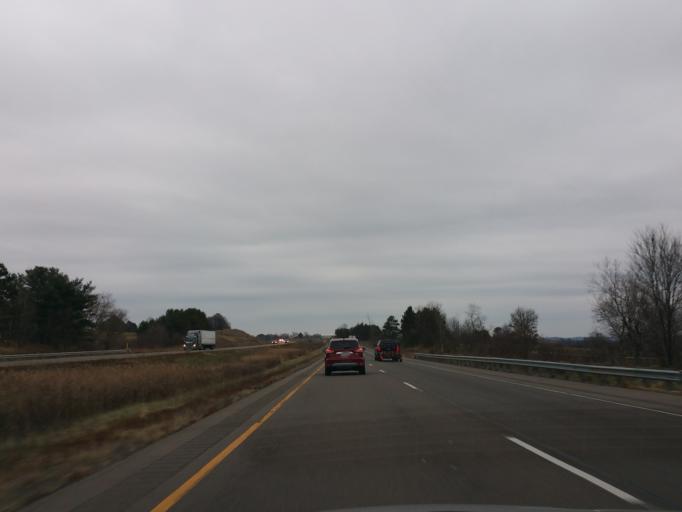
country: US
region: Wisconsin
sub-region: Trempealeau County
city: Blair
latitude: 44.4187
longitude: -91.0522
